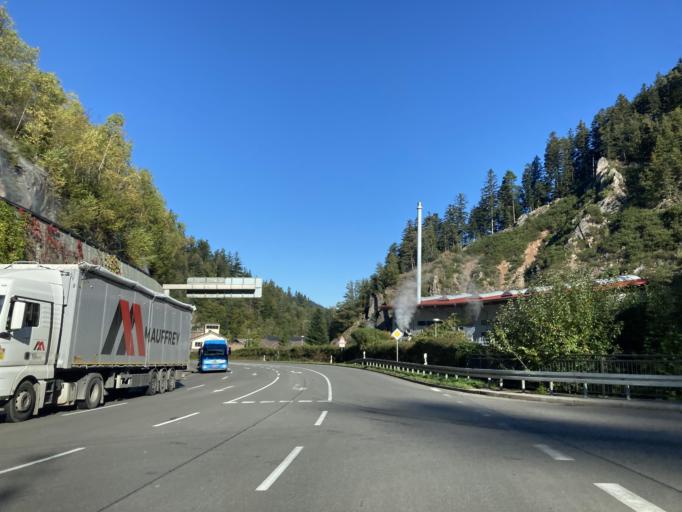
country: DE
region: Baden-Wuerttemberg
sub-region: Freiburg Region
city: Triberg im Schwarzwald
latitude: 48.1598
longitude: 8.2390
